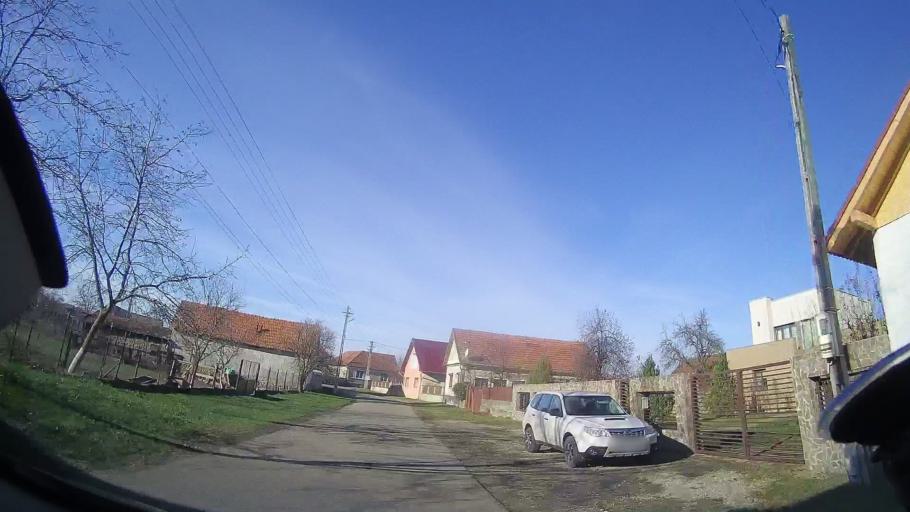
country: RO
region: Bihor
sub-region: Comuna Auseu
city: Auseu
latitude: 47.0250
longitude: 22.4899
